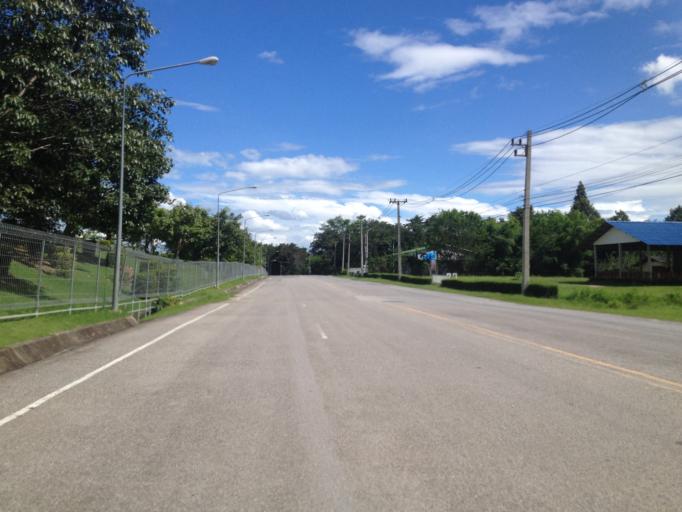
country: TH
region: Chiang Mai
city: Hang Dong
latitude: 18.7459
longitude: 98.9221
